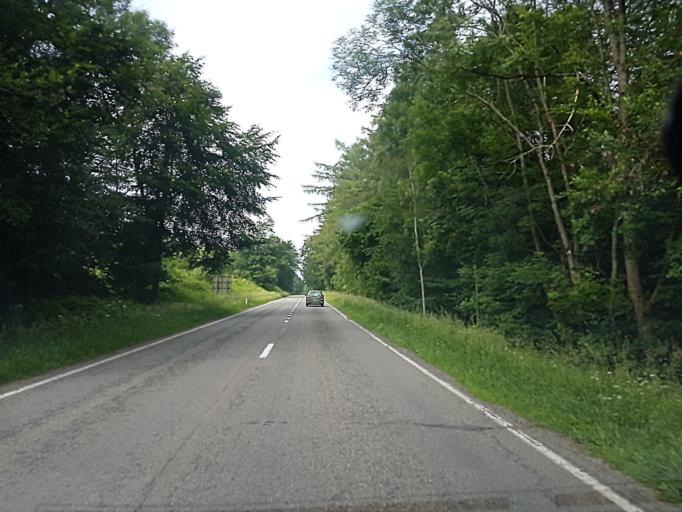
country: BE
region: Wallonia
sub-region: Province du Luxembourg
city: Manhay
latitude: 50.2773
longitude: 5.6936
